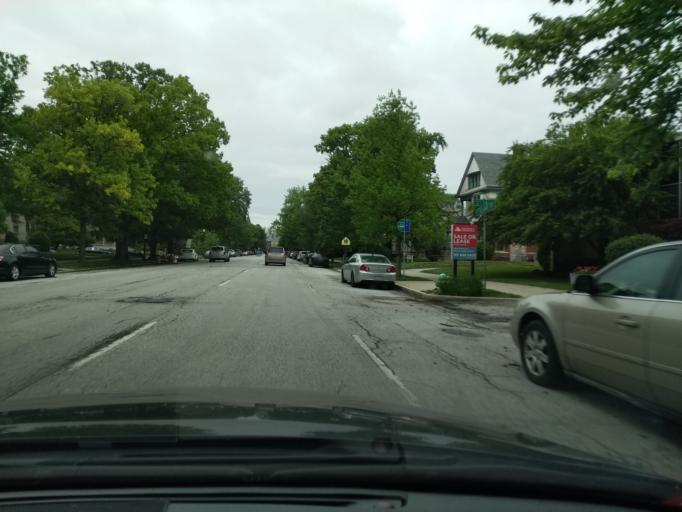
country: US
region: Indiana
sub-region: Marion County
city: Indianapolis
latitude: 39.7854
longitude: -86.1540
